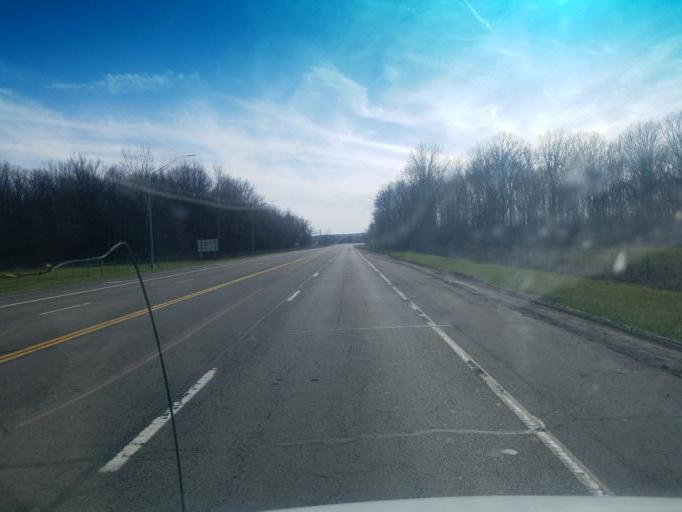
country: US
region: Ohio
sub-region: Champaign County
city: North Lewisburg
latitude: 40.3319
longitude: -83.5595
